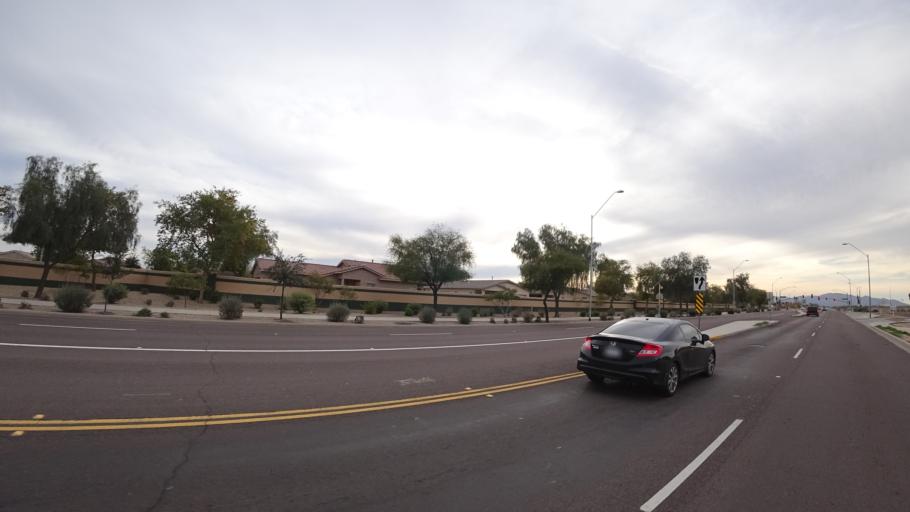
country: US
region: Arizona
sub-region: Maricopa County
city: Surprise
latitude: 33.6238
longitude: -112.3568
